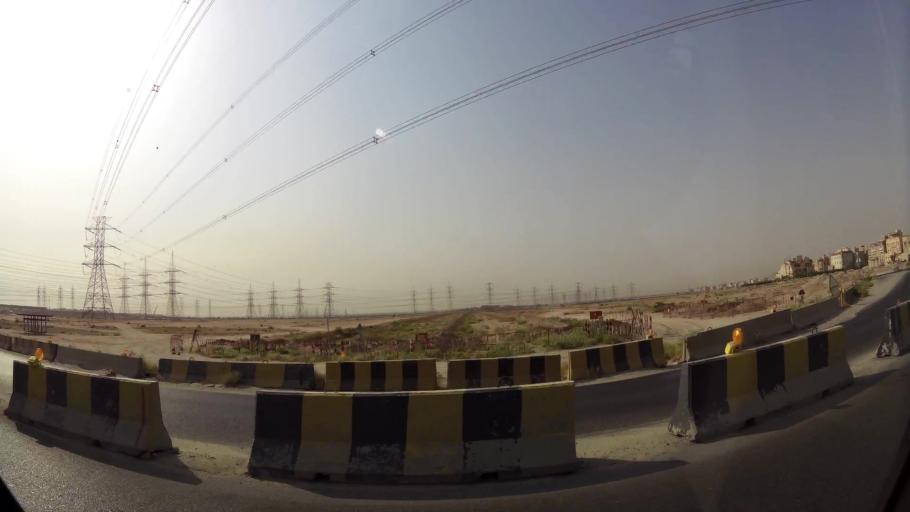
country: KW
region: Muhafazat al Jahra'
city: Al Jahra'
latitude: 29.3400
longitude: 47.7913
